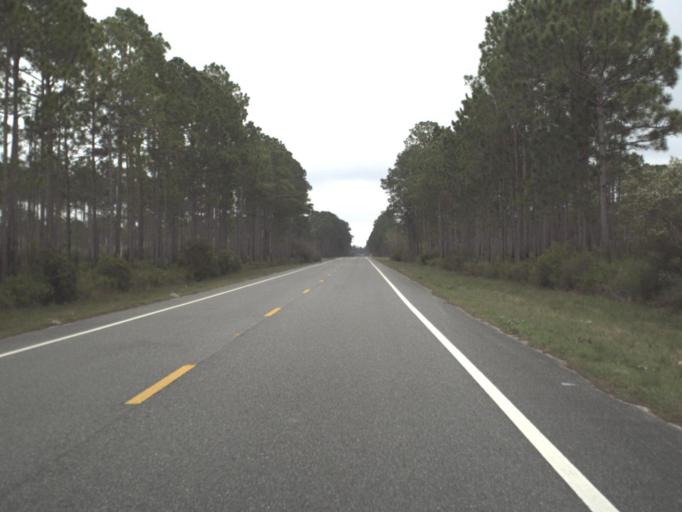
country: US
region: Florida
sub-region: Franklin County
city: Eastpoint
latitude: 29.8137
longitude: -84.8444
